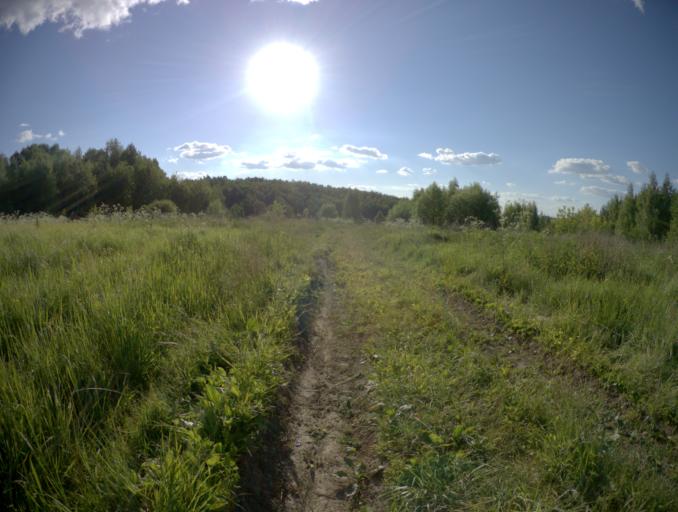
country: RU
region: Vladimir
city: Stavrovo
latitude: 56.2458
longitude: 40.0859
